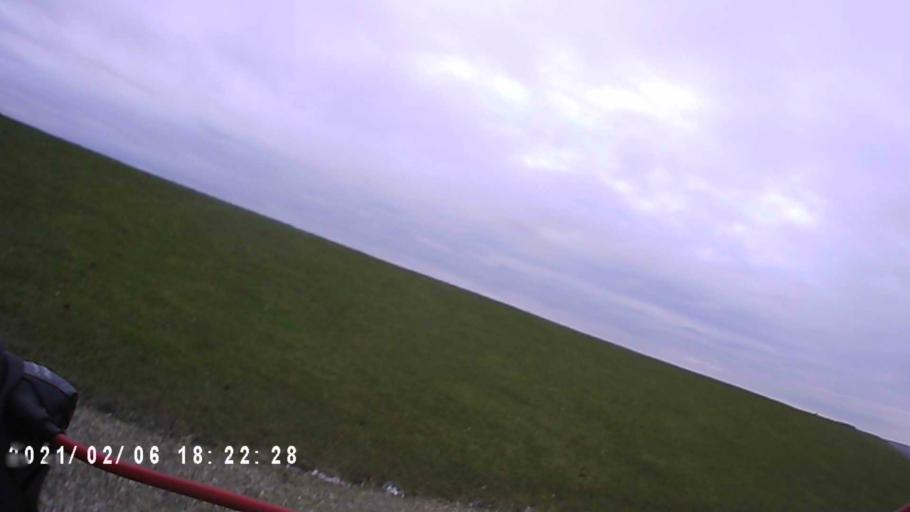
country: DE
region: Lower Saxony
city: Borkum
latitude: 53.4637
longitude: 6.7184
